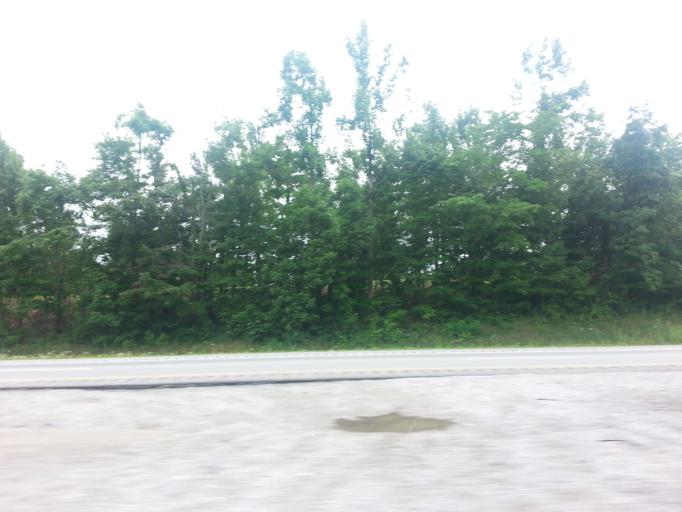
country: US
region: Tennessee
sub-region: Putnam County
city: Monterey
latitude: 36.1361
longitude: -85.3242
